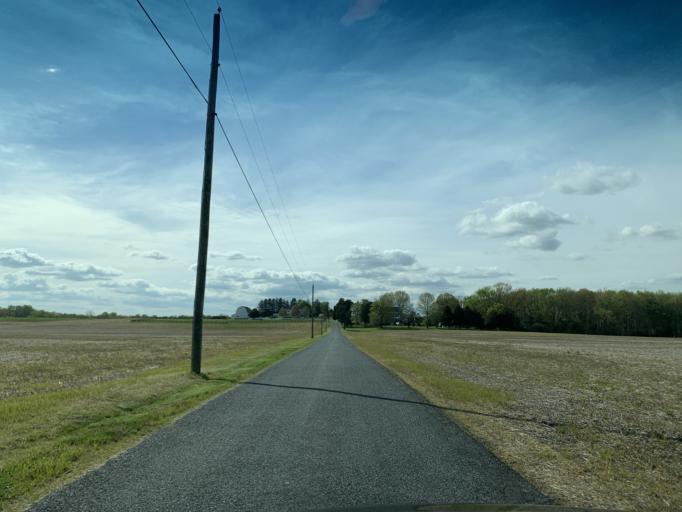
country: US
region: Maryland
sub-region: Harford County
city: Perryman
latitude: 39.4684
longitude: -76.2092
